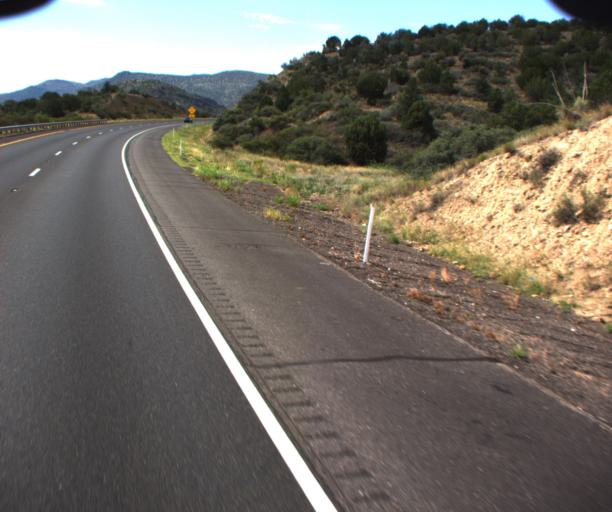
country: US
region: Arizona
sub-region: Yavapai County
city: Camp Verde
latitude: 34.5455
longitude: -111.9088
